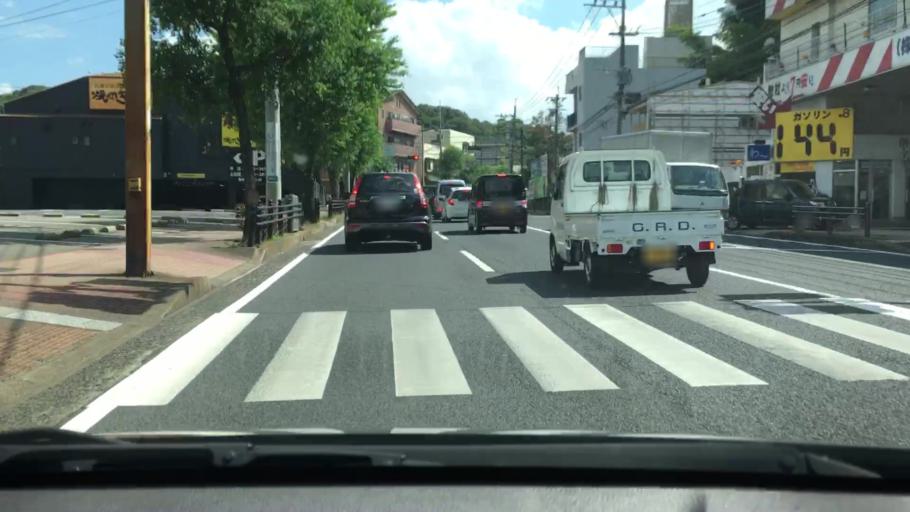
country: JP
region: Nagasaki
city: Sasebo
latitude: 33.2047
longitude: 129.7211
